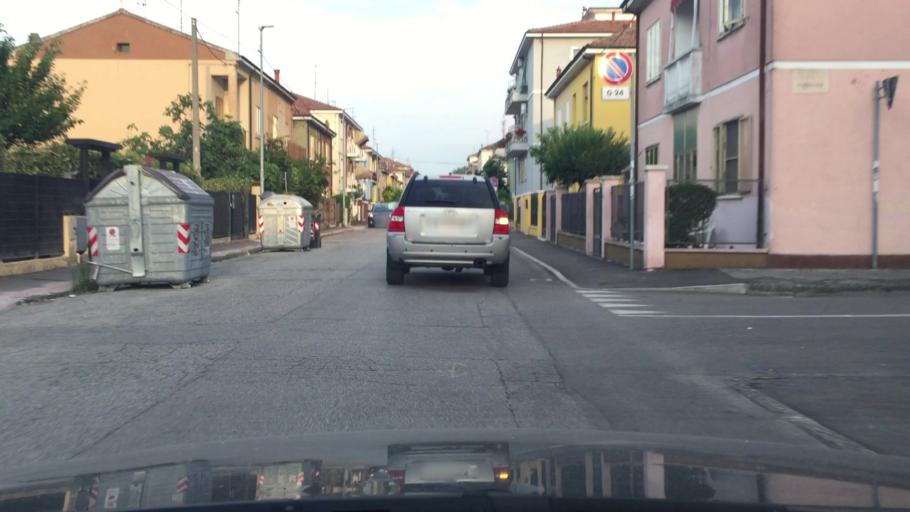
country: IT
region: Emilia-Romagna
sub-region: Provincia di Ferrara
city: Ferrara
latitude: 44.8222
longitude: 11.6104
